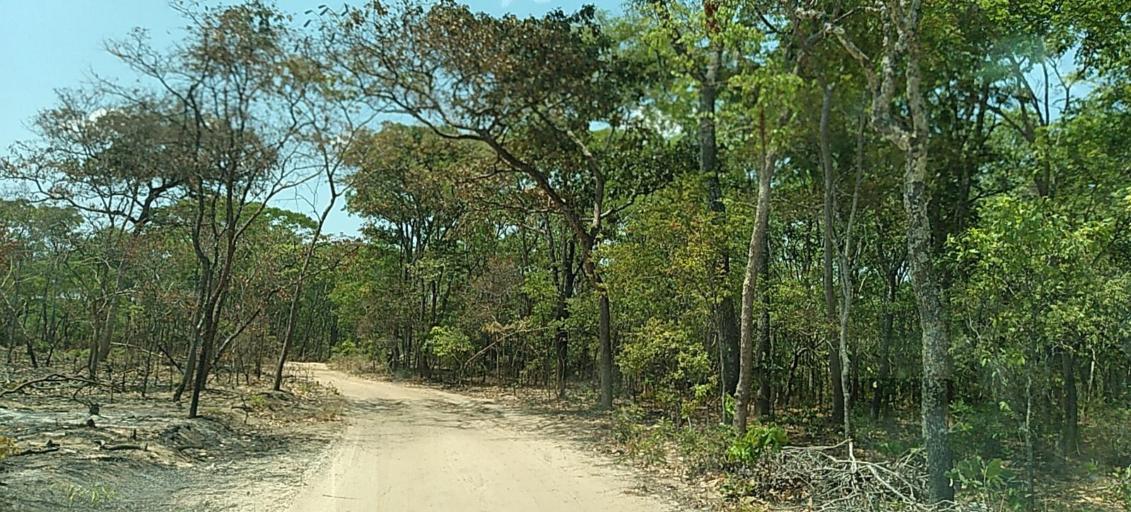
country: ZM
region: Copperbelt
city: Mpongwe
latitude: -13.6436
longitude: 28.4844
